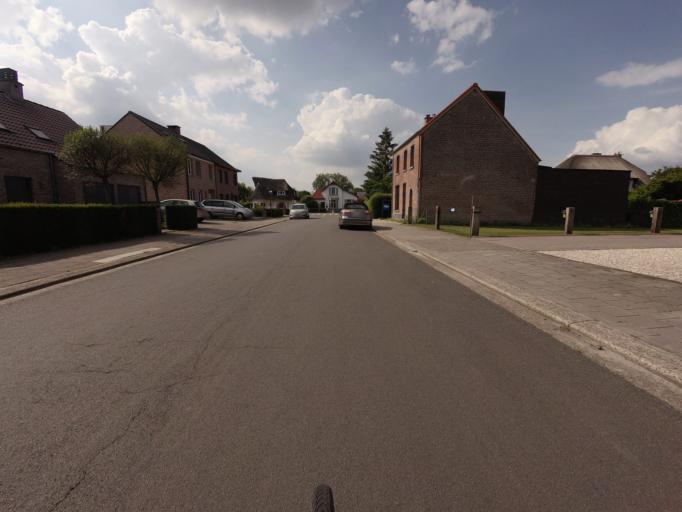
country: BE
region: Flanders
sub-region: Provincie Antwerpen
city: Lint
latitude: 51.1330
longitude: 4.4854
